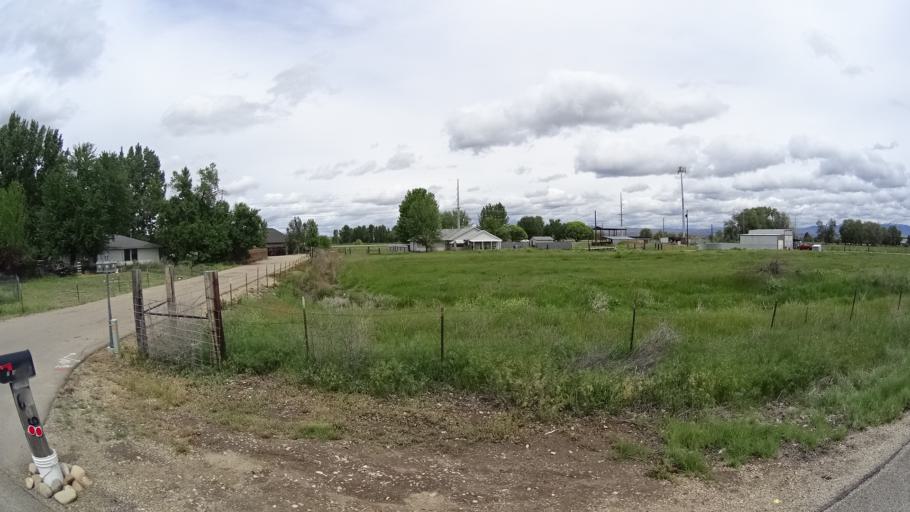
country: US
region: Idaho
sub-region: Ada County
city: Star
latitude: 43.6899
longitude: -116.4571
